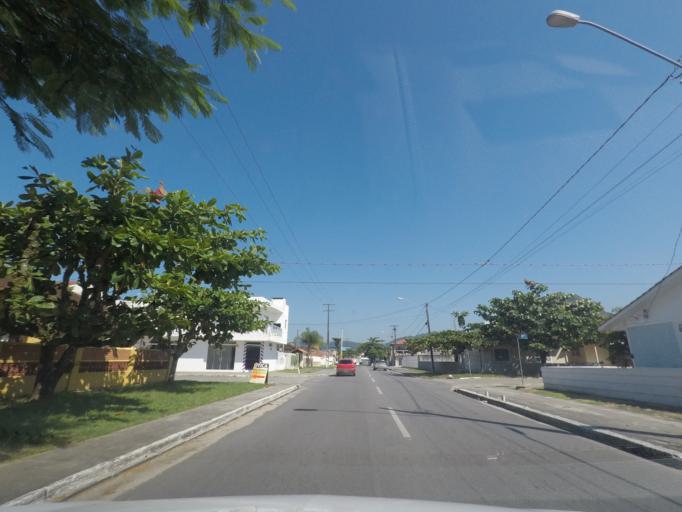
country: BR
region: Parana
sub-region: Guaratuba
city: Guaratuba
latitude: -25.8140
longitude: -48.5349
